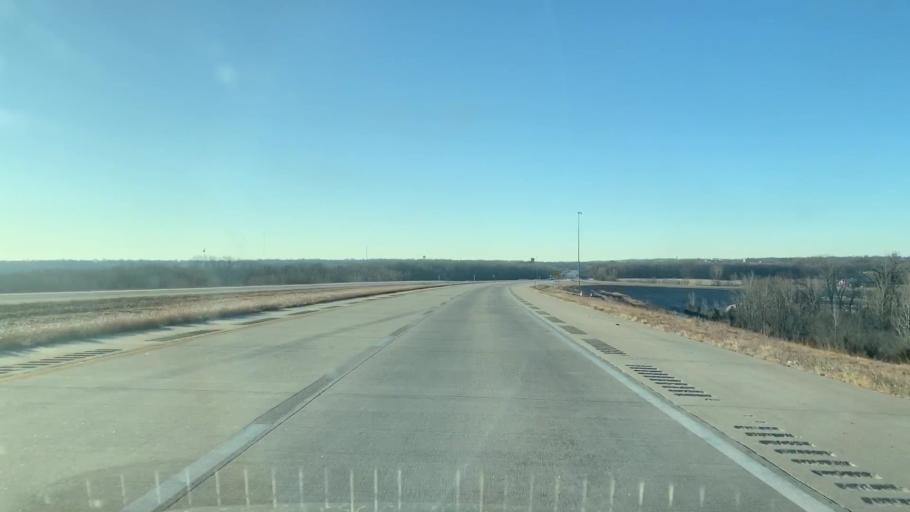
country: US
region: Kansas
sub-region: Bourbon County
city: Fort Scott
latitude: 37.8610
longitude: -94.7029
